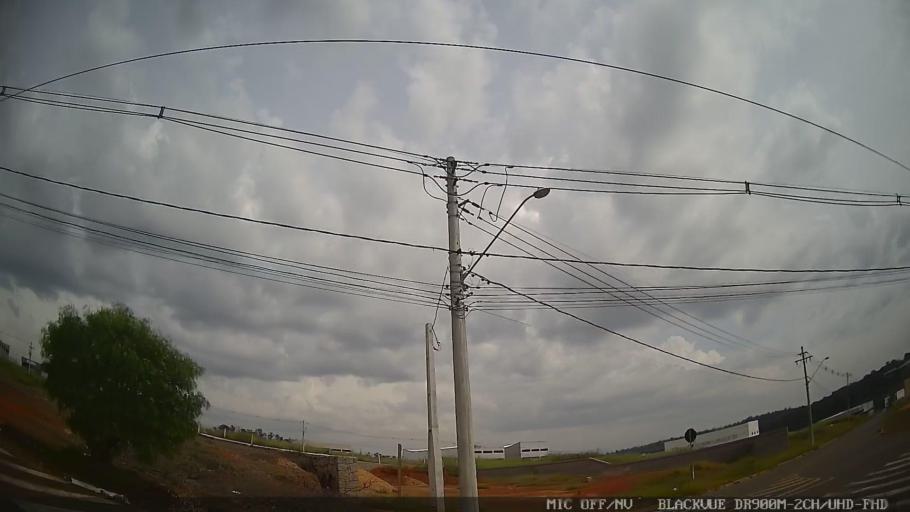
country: BR
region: Sao Paulo
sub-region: Indaiatuba
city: Indaiatuba
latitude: -23.1225
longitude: -47.2680
